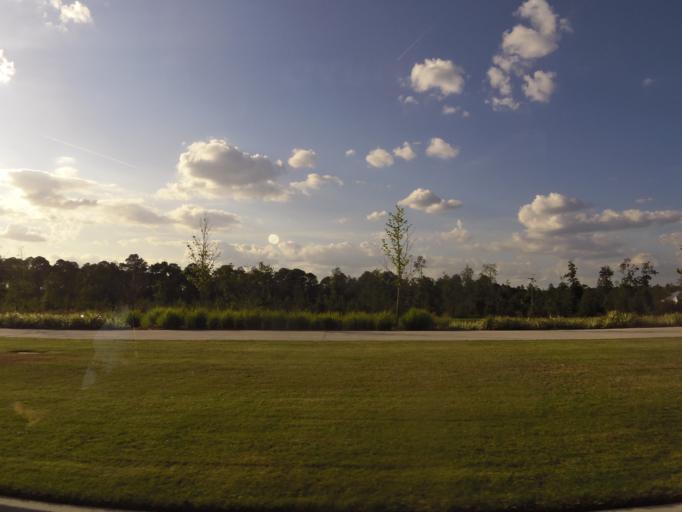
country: US
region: Florida
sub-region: Saint Johns County
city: Palm Valley
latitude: 30.0844
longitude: -81.4856
